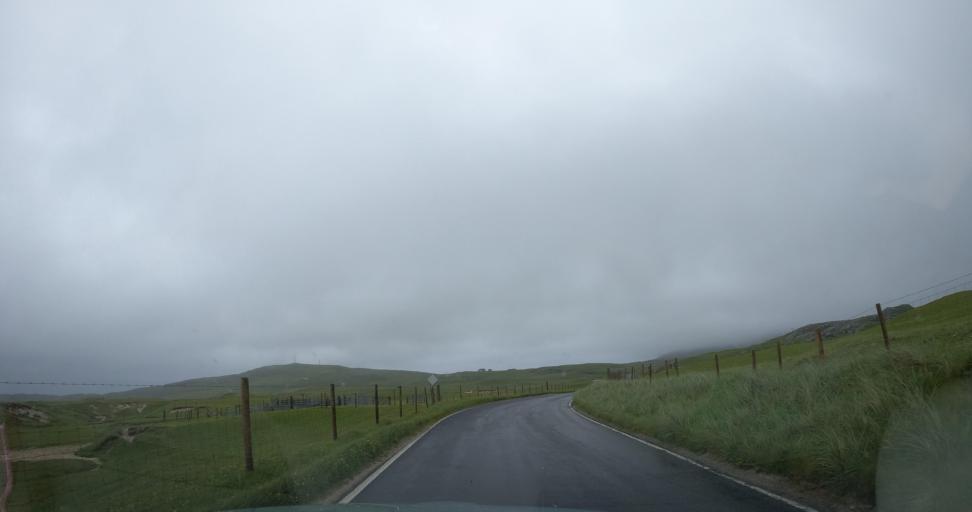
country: GB
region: Scotland
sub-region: Eilean Siar
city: Barra
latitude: 56.9995
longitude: -7.5049
